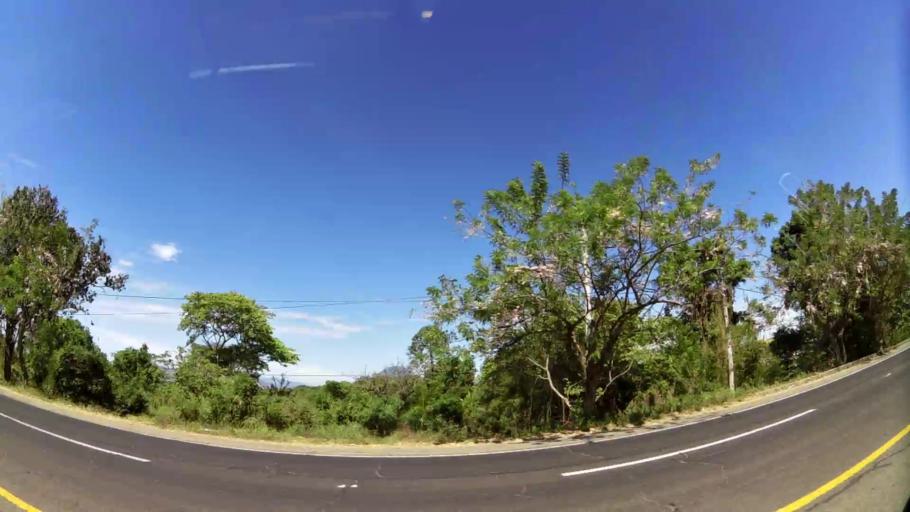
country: SV
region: Santa Ana
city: Chalchuapa
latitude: 13.9727
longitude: -89.7130
